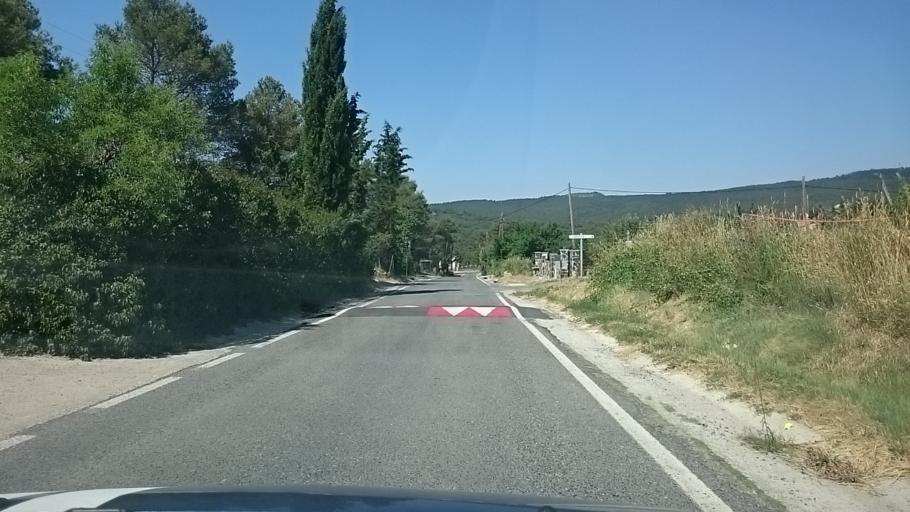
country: ES
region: Catalonia
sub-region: Provincia de Tarragona
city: Querol
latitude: 41.3966
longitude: 1.4578
